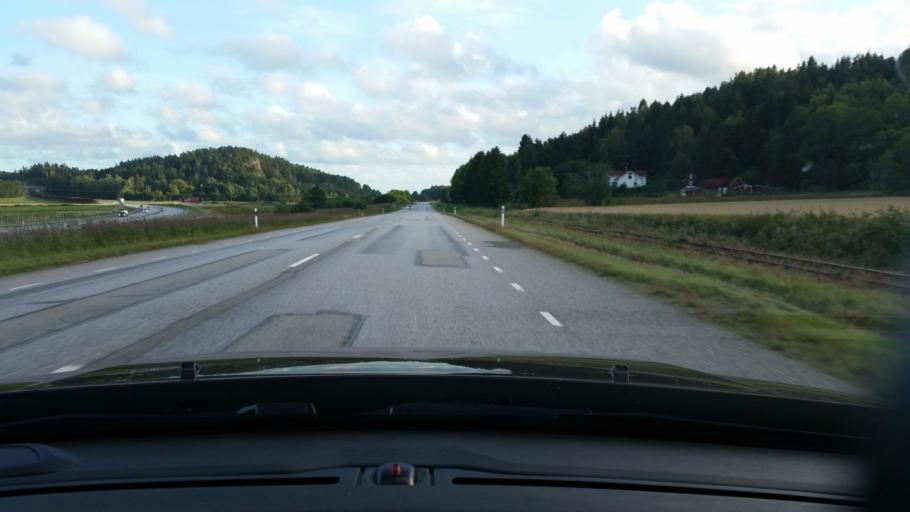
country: SE
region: Vaestra Goetaland
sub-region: Lilla Edets Kommun
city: Lodose
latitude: 58.0767
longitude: 12.1540
